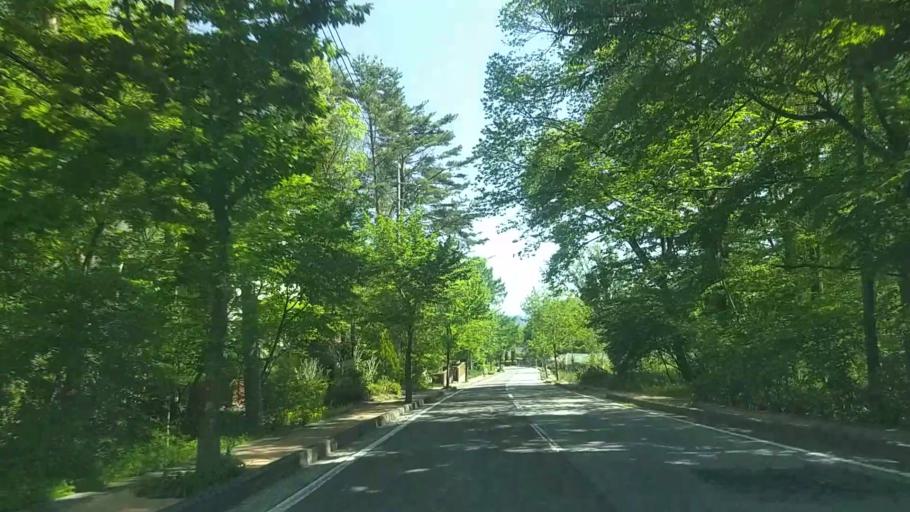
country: JP
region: Yamanashi
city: Nirasaki
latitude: 35.8992
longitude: 138.4368
